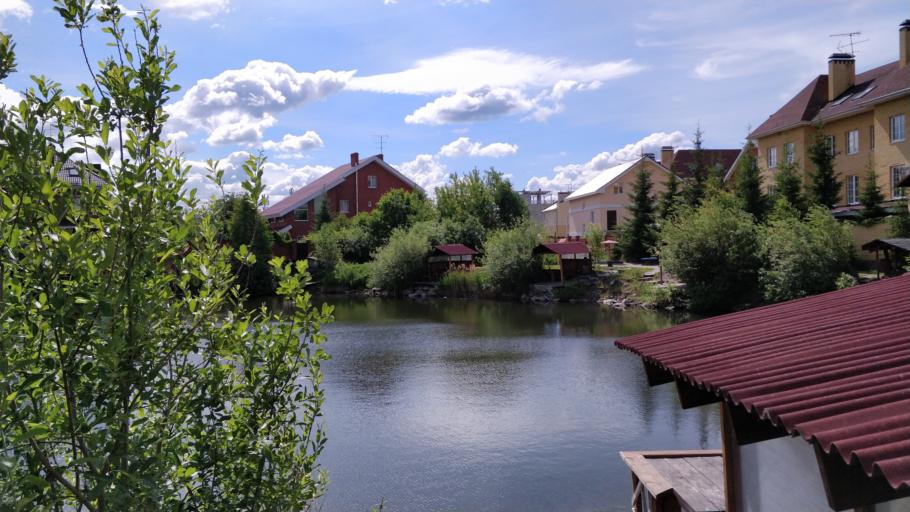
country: RU
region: Sverdlovsk
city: Sovkhoznyy
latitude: 56.7856
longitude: 60.5270
